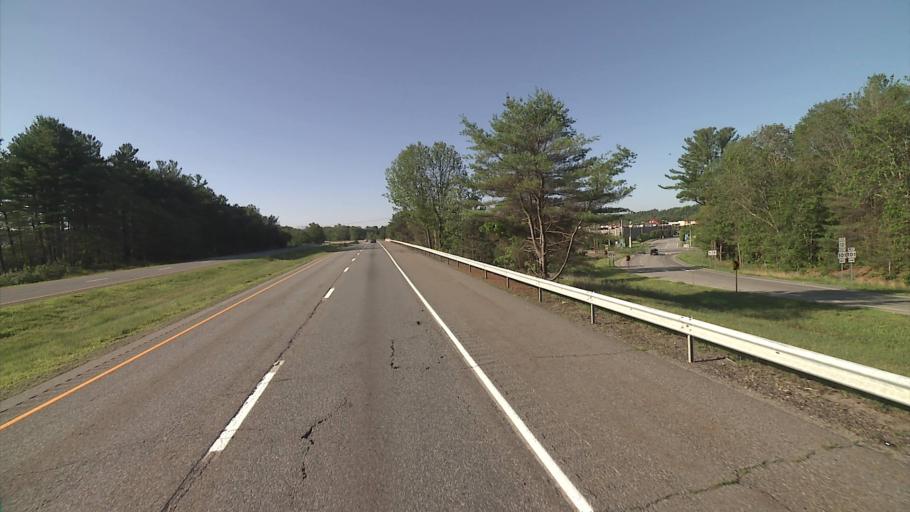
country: US
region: Connecticut
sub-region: Windham County
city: Killingly Center
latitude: 41.8444
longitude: -71.8794
